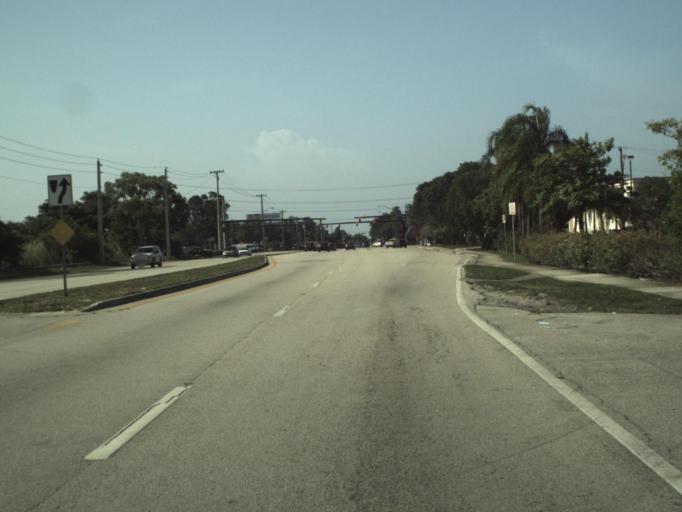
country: US
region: Florida
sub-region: Broward County
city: Tedder
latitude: 26.2728
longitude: -80.1356
